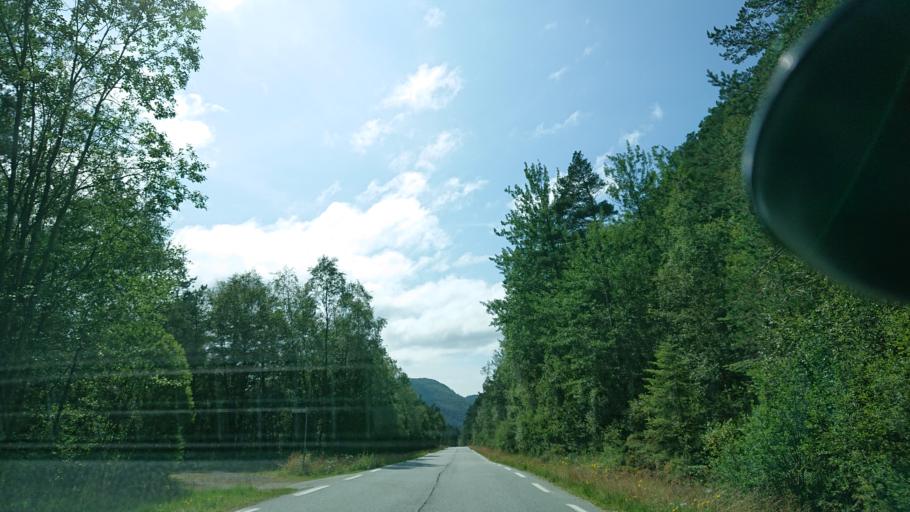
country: NO
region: Rogaland
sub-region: Hjelmeland
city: Hjelmelandsvagen
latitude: 59.2332
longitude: 6.2438
